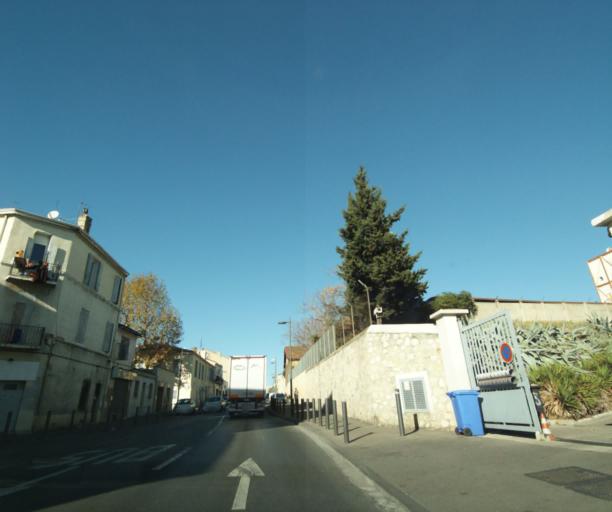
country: FR
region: Provence-Alpes-Cote d'Azur
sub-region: Departement des Bouches-du-Rhone
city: Marseille 14
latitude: 43.3339
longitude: 5.3640
